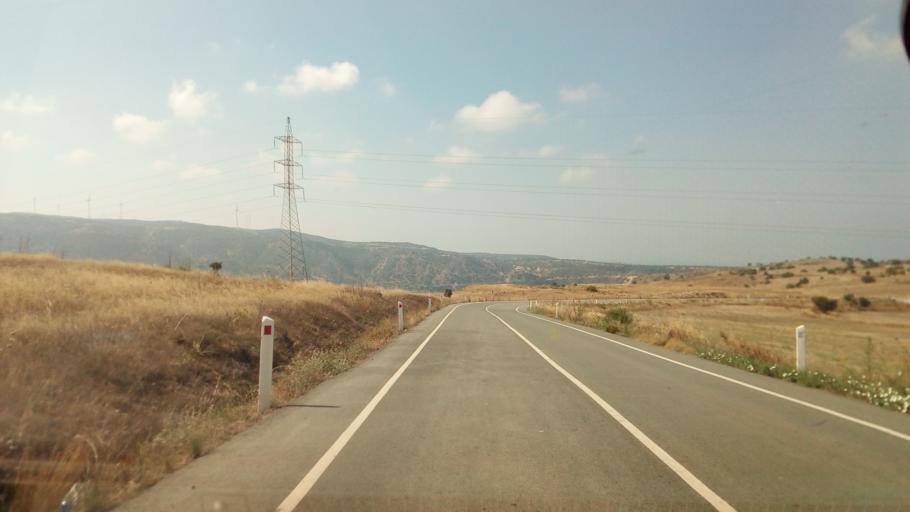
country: CY
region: Limassol
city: Pissouri
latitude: 34.7506
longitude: 32.5955
